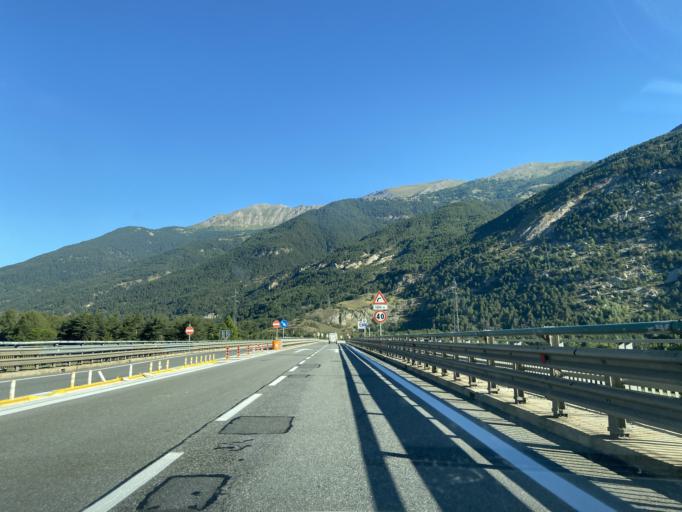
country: IT
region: Piedmont
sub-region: Provincia di Torino
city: Oulx
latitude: 45.0362
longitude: 6.8177
